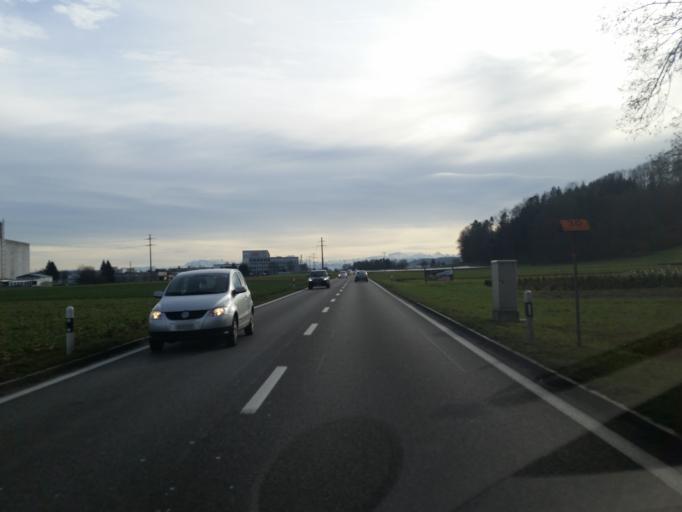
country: CH
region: Aargau
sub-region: Bezirk Bremgarten
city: Dottikon
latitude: 47.3792
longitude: 8.2183
